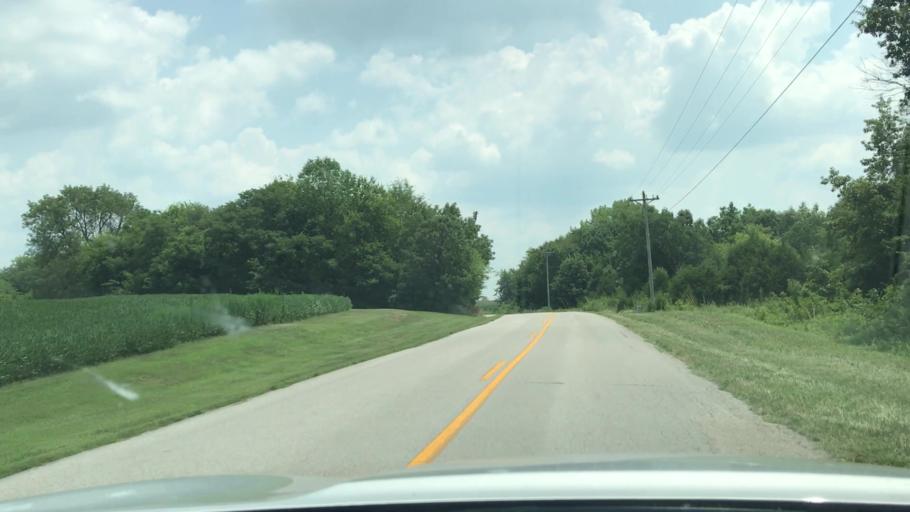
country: US
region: Kentucky
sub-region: Todd County
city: Elkton
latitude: 36.7620
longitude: -87.1050
